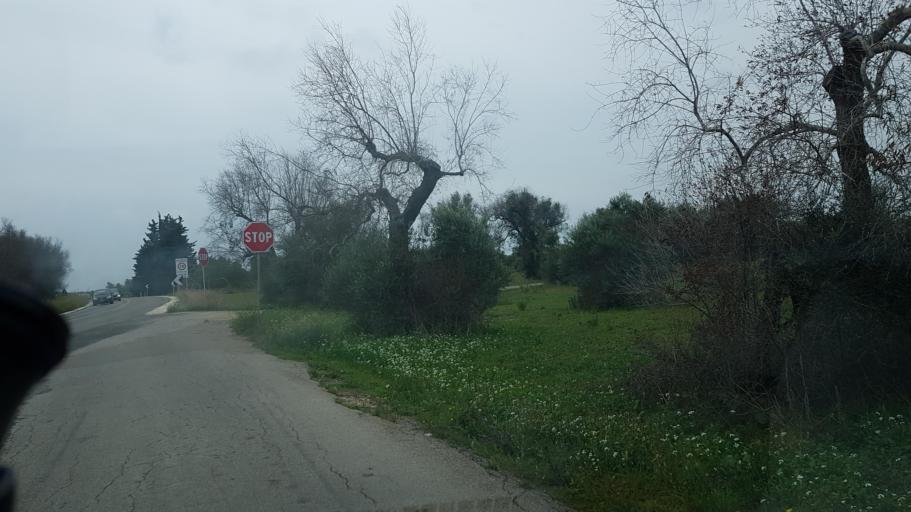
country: IT
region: Apulia
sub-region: Provincia di Brindisi
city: San Pietro Vernotico
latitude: 40.5162
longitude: 18.0116
